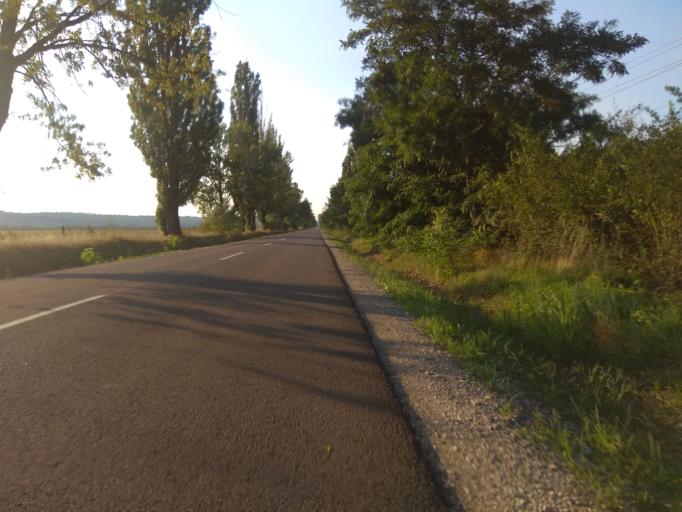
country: HU
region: Borsod-Abauj-Zemplen
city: Nyekladhaza
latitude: 47.9700
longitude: 20.8541
